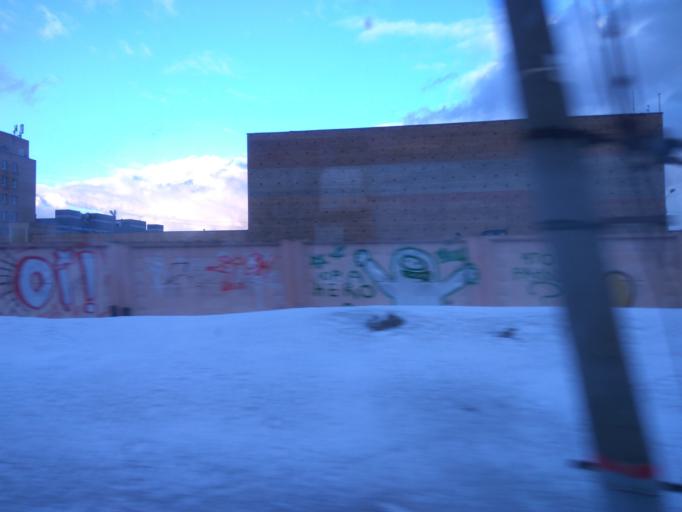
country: RU
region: Moscow
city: Nagornyy
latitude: 55.6454
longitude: 37.6237
